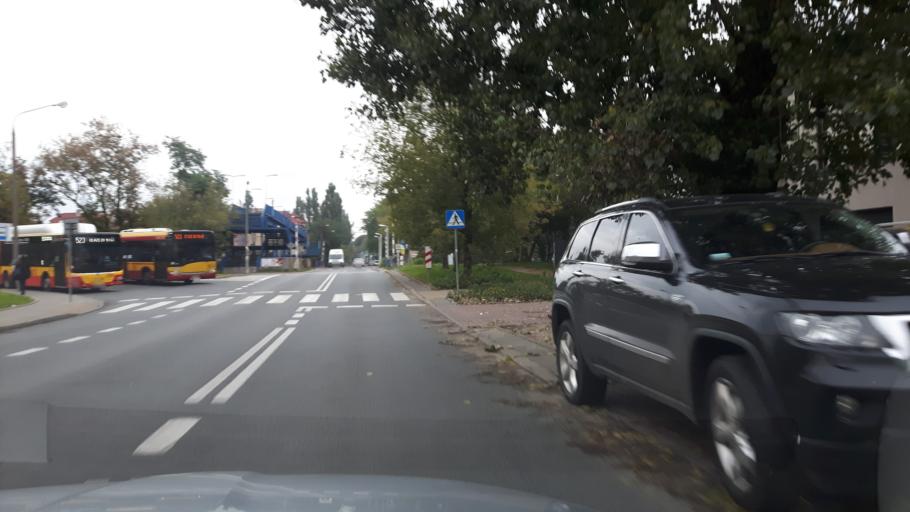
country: PL
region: Masovian Voivodeship
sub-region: Warszawa
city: Praga Poludnie
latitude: 52.2486
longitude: 21.1075
